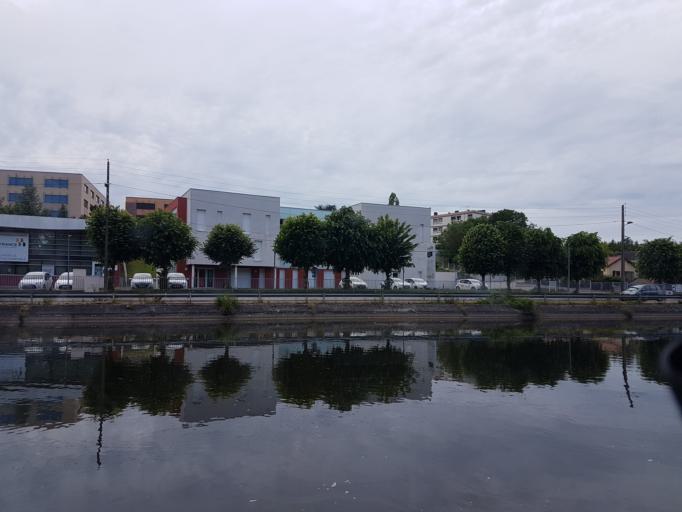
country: FR
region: Bourgogne
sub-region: Departement de l'Yonne
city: Auxerre
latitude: 47.8083
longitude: 3.5762
